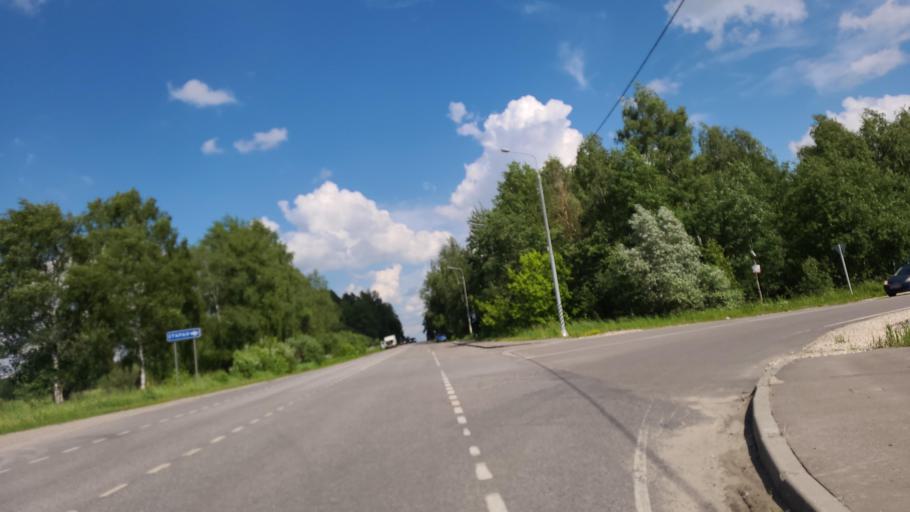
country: RU
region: Moskovskaya
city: Konobeyevo
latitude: 55.4020
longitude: 38.6748
